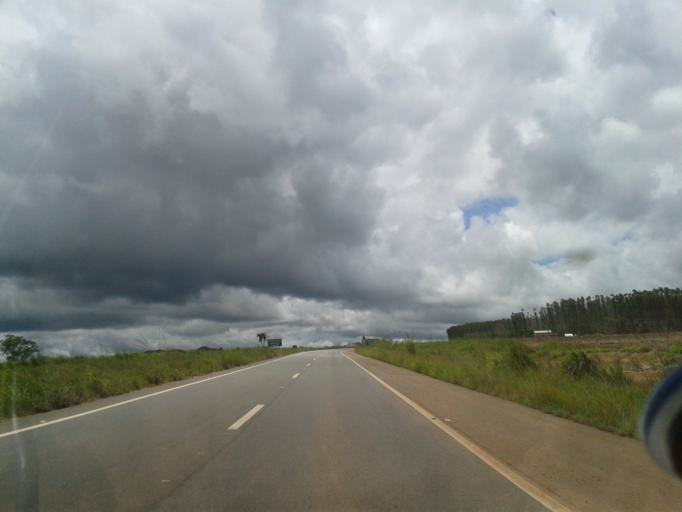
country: BR
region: Goias
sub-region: Goias
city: Goias
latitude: -16.0039
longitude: -50.0210
